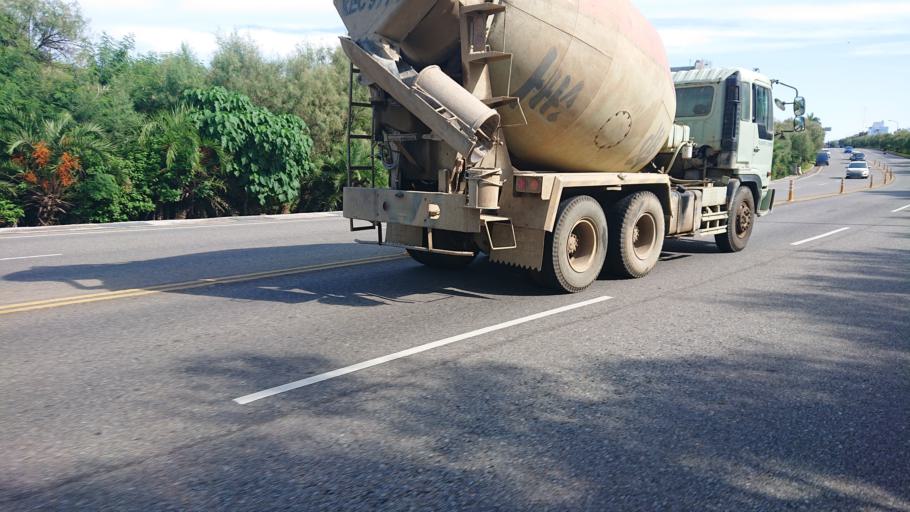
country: TW
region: Taiwan
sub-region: Penghu
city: Ma-kung
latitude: 23.5404
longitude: 119.6051
